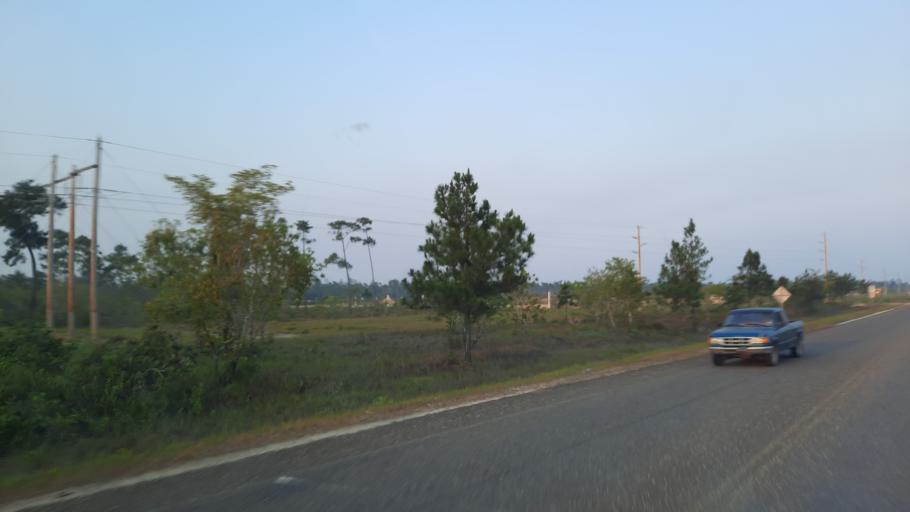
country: BZ
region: Stann Creek
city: Placencia
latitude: 16.5326
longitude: -88.4739
